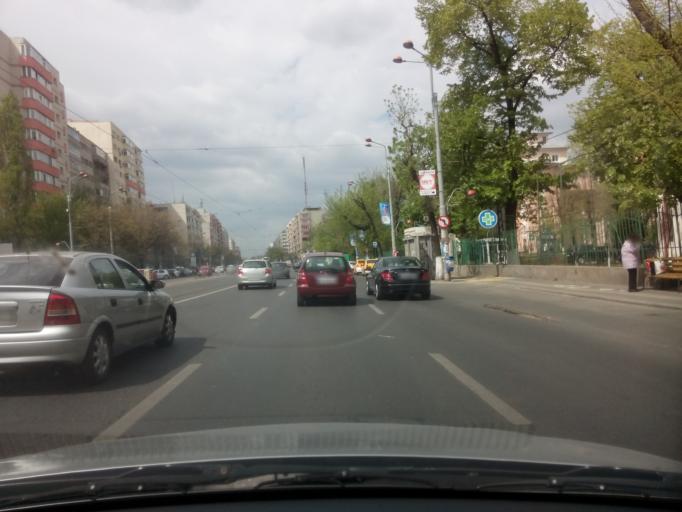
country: RO
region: Bucuresti
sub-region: Municipiul Bucuresti
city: Bucharest
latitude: 44.4528
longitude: 26.1146
